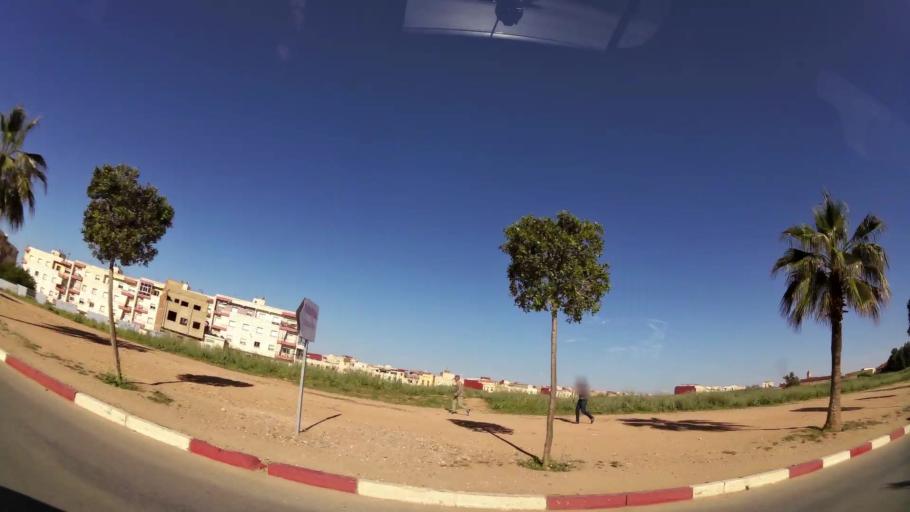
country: MA
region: Meknes-Tafilalet
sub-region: Meknes
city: Meknes
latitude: 33.8784
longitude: -5.5740
